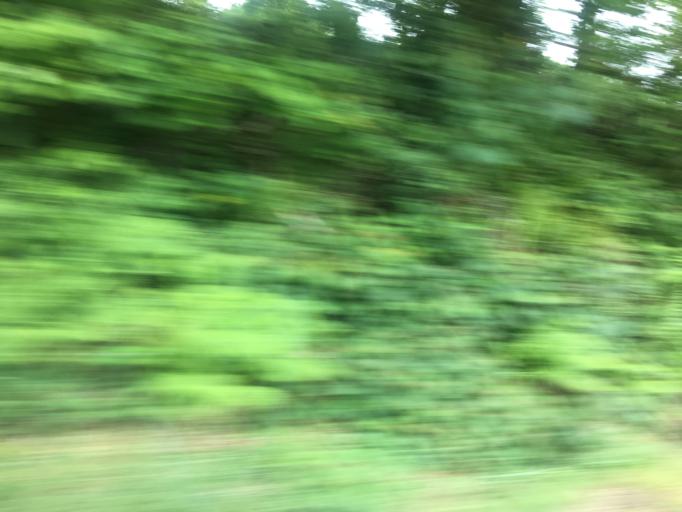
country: GB
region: Wales
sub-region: Carmarthenshire
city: Llansawel
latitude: 52.0768
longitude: -4.0101
